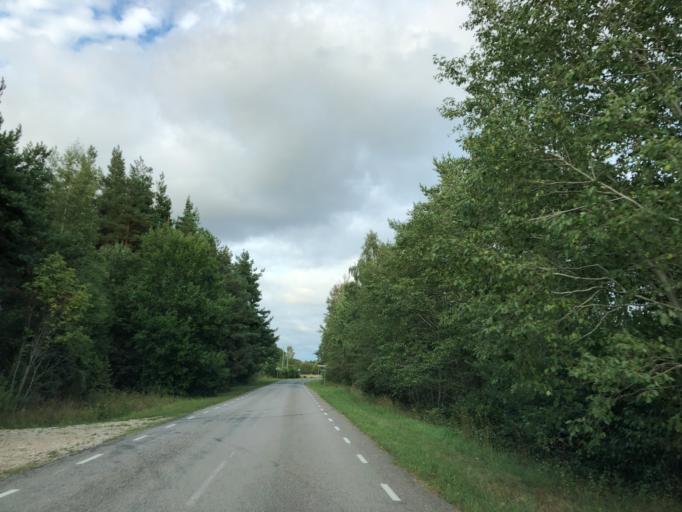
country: EE
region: Hiiumaa
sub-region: Kaerdla linn
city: Kardla
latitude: 58.7879
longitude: 22.7974
